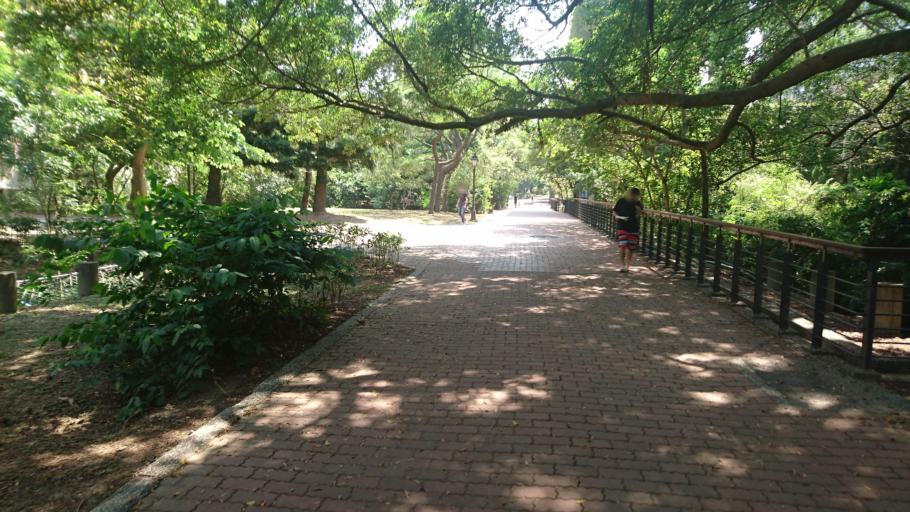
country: TW
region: Taiwan
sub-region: Hsinchu
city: Hsinchu
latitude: 24.7947
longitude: 120.9927
